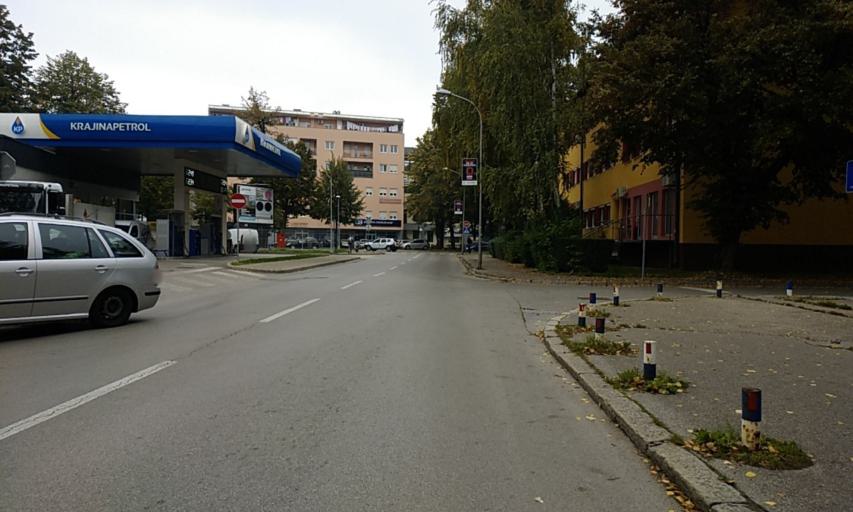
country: BA
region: Republika Srpska
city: Banja Luka
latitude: 44.7733
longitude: 17.1980
